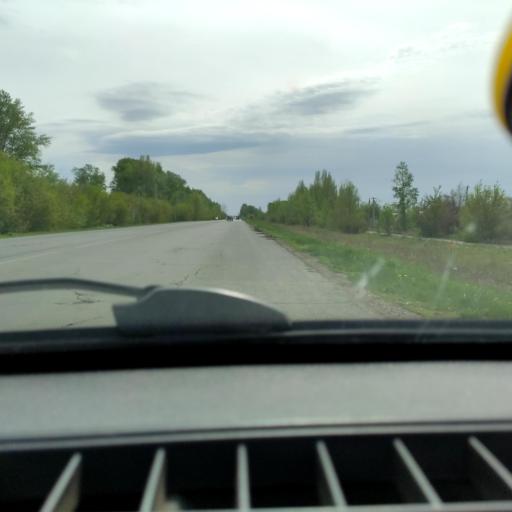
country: RU
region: Samara
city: Tol'yatti
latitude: 53.7021
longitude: 49.4210
